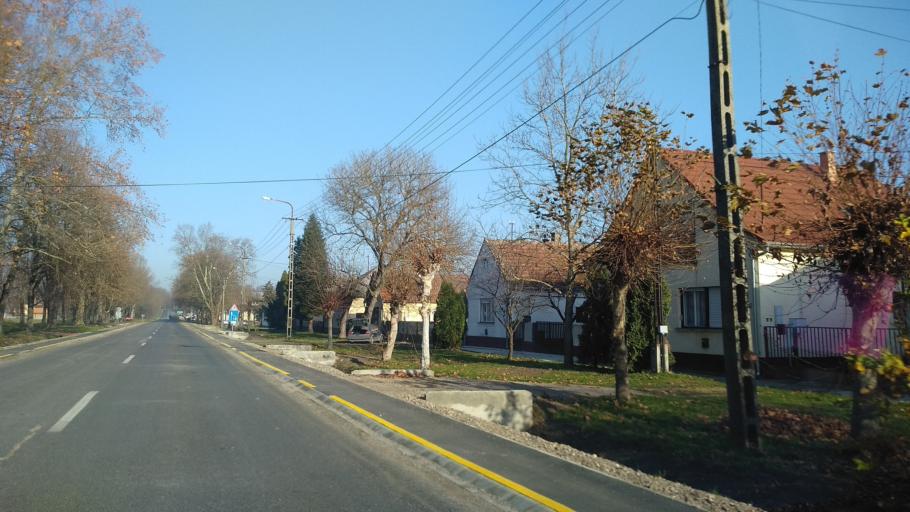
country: HU
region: Somogy
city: Barcs
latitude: 45.9703
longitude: 17.4588
